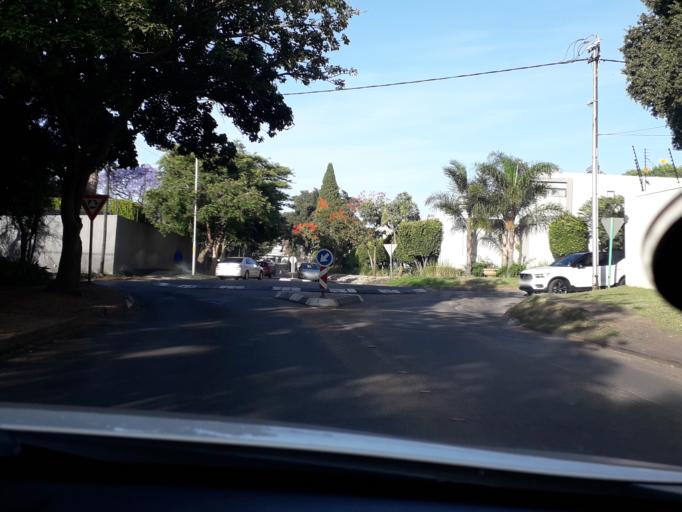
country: ZA
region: Gauteng
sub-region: City of Johannesburg Metropolitan Municipality
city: Johannesburg
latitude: -26.1259
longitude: 28.0530
